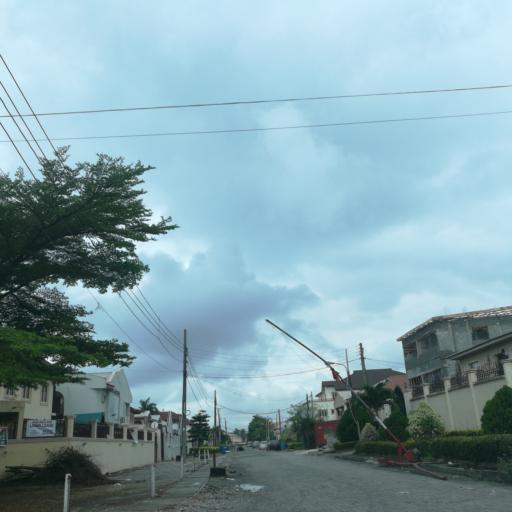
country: NG
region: Lagos
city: Ikoyi
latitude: 6.4415
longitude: 3.4623
